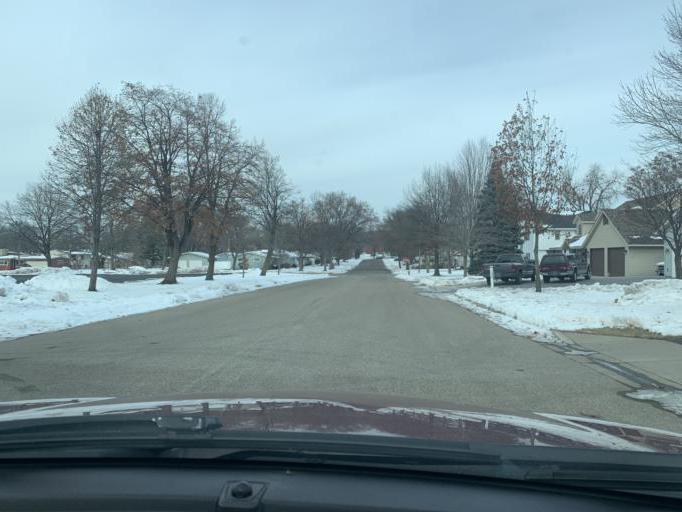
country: US
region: Minnesota
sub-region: Washington County
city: Saint Paul Park
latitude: 44.8414
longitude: -92.9856
